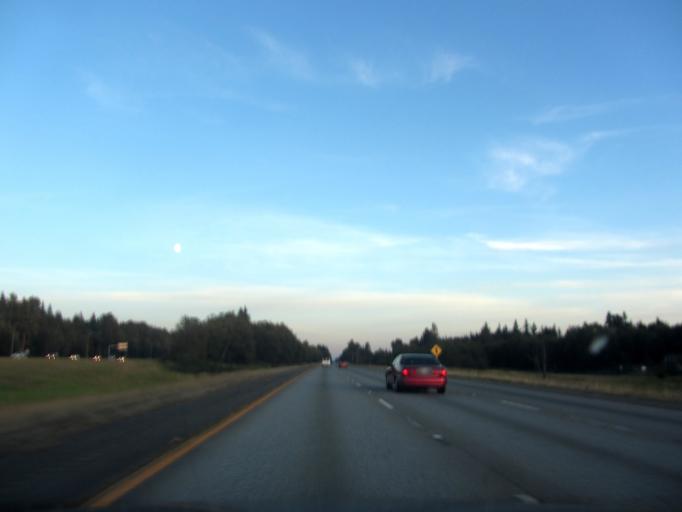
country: US
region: Washington
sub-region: Snohomish County
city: Stanwood
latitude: 48.2669
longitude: -122.2688
